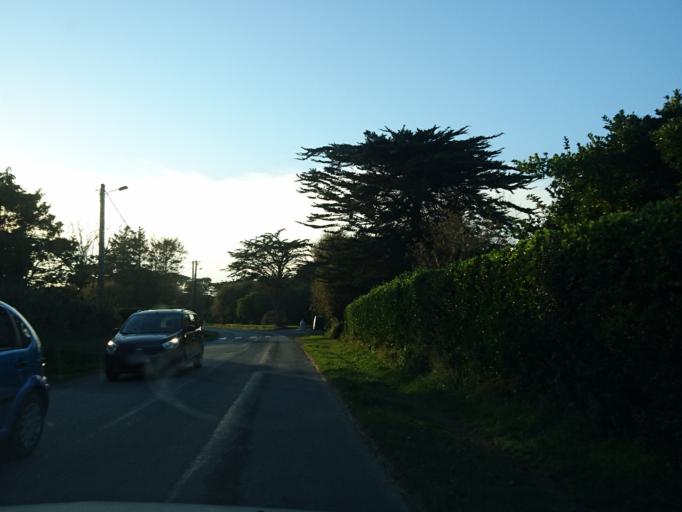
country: FR
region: Brittany
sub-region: Departement du Finistere
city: Landunvez
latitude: 48.5269
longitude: -4.7509
